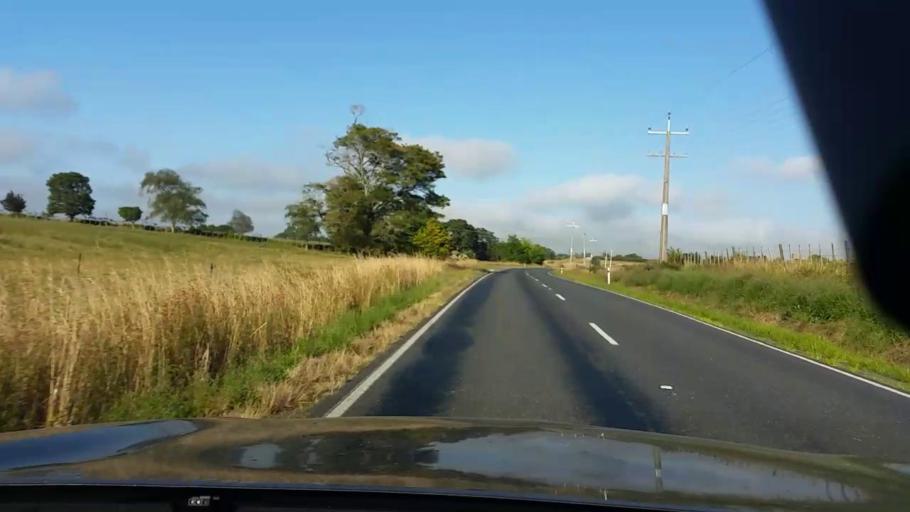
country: NZ
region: Waikato
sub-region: Hamilton City
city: Hamilton
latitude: -37.5914
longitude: 175.3841
